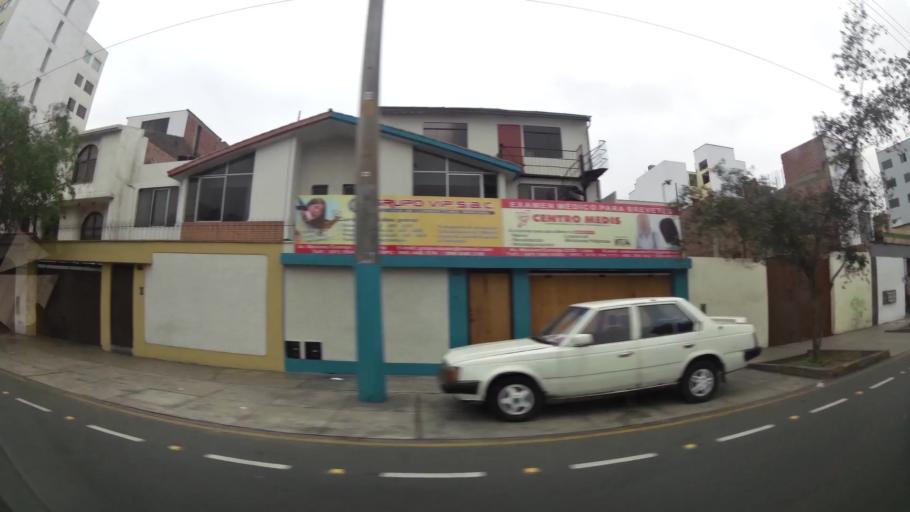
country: PE
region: Callao
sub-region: Callao
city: Callao
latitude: -12.0681
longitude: -77.0760
